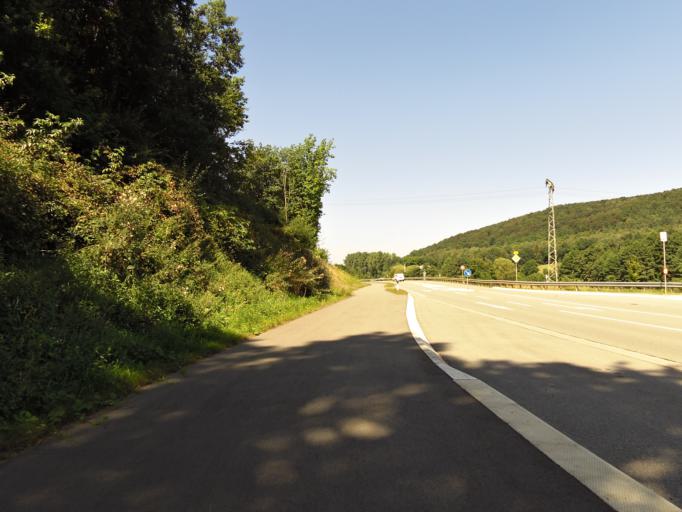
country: DE
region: Rheinland-Pfalz
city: Munchweiler an der Alsenz
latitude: 49.5253
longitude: 7.8903
